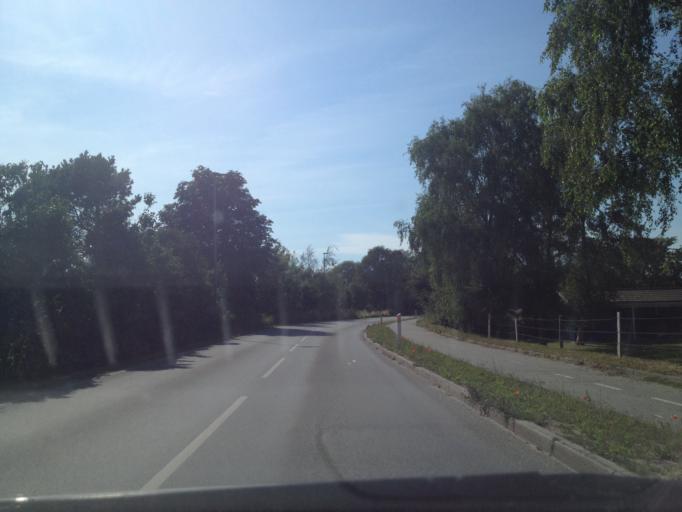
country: DK
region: Central Jutland
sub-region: Samso Kommune
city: Tranebjerg
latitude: 55.8618
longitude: 10.5542
